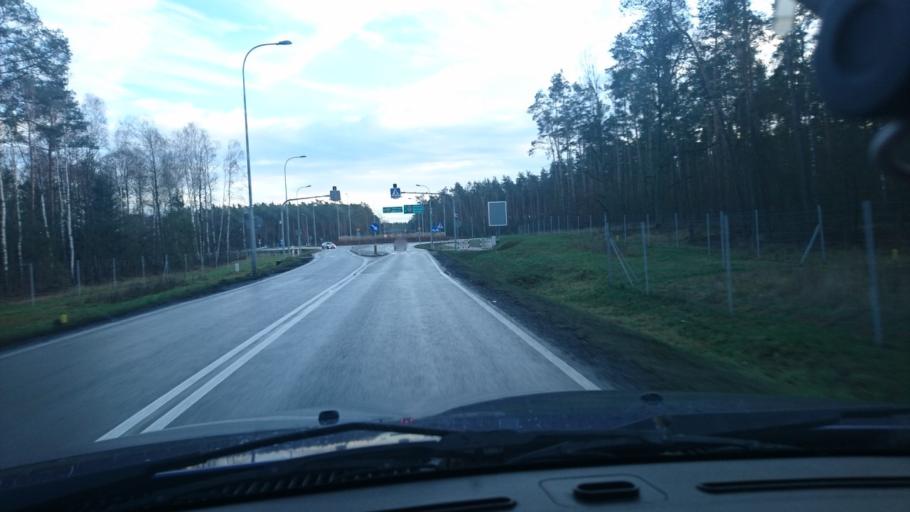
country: PL
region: Greater Poland Voivodeship
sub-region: Powiat kepinski
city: Kepno
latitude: 51.3326
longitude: 17.9576
